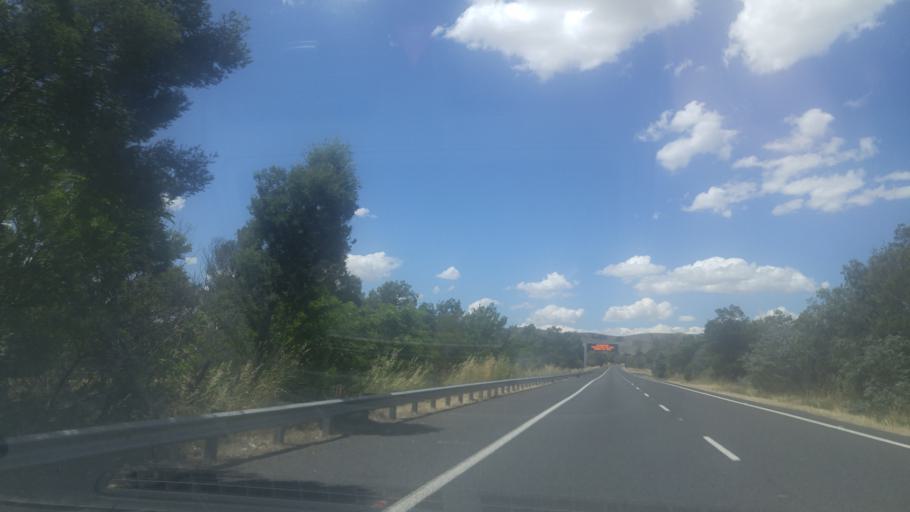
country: AU
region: New South Wales
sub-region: Yass Valley
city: Yass
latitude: -34.7857
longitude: 148.7040
